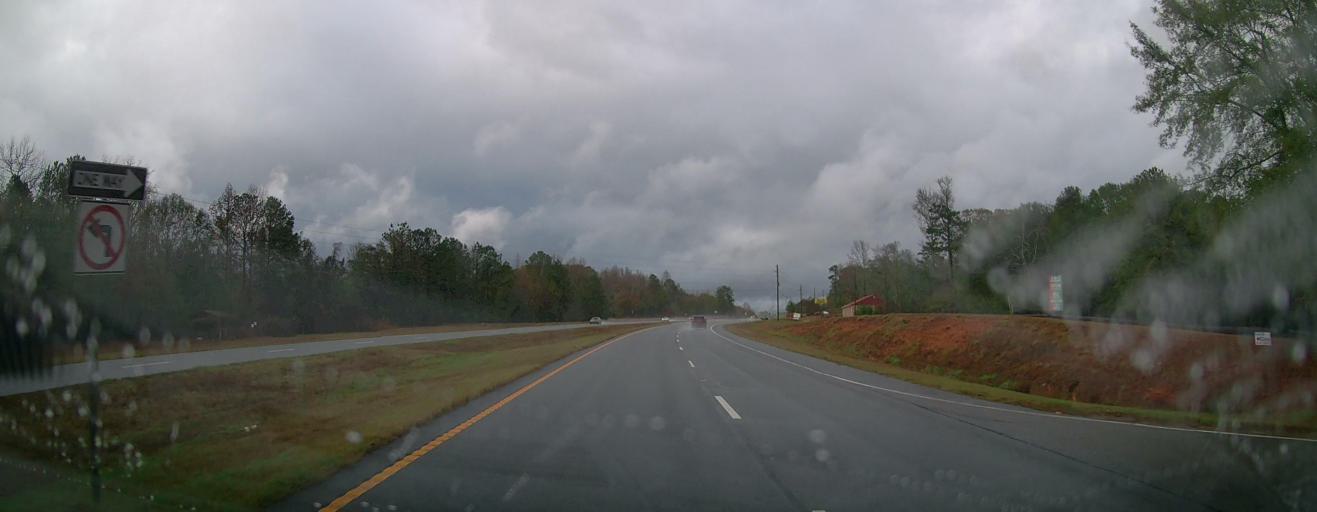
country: US
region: Georgia
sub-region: Clarke County
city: Country Club Estates
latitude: 34.0289
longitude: -83.4012
